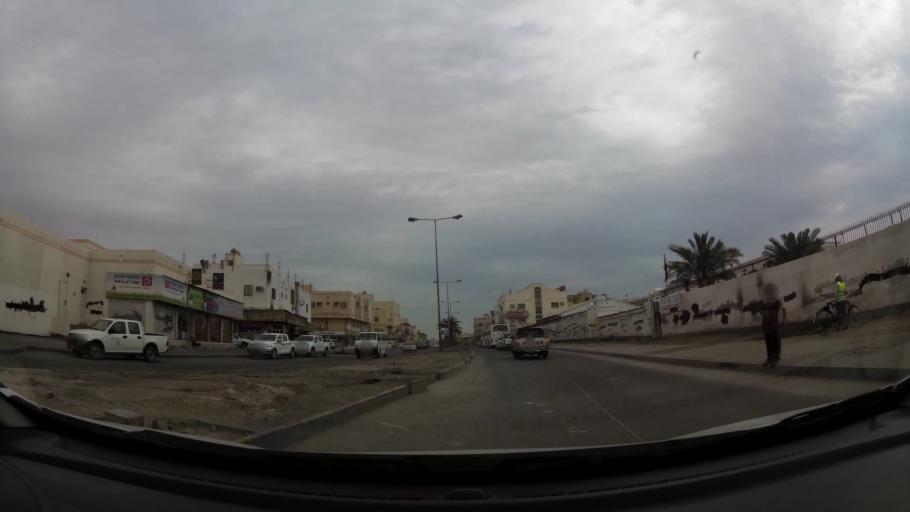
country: BH
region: Northern
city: Sitrah
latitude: 26.1613
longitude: 50.6165
